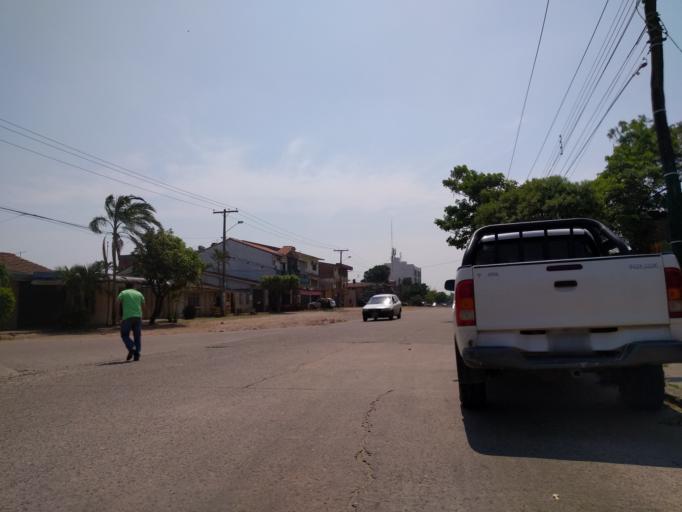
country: BO
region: Santa Cruz
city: Santa Cruz de la Sierra
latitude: -17.7929
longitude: -63.1557
